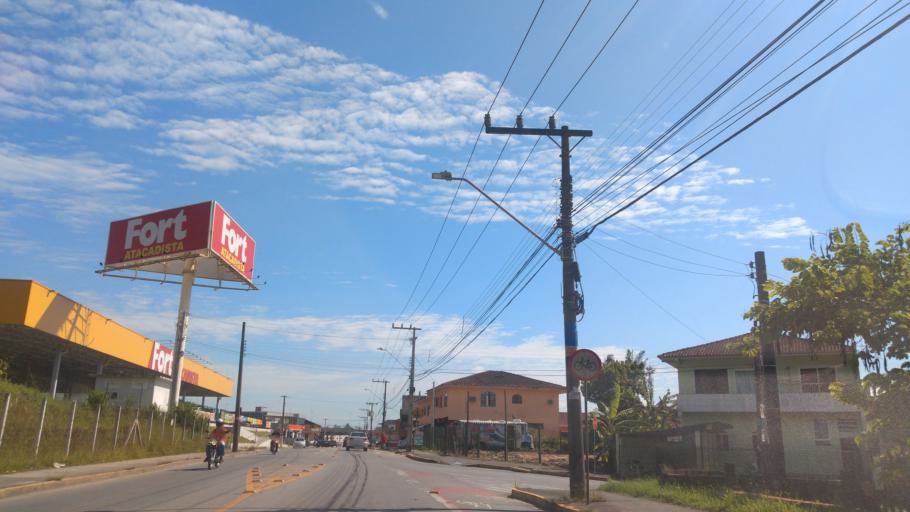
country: BR
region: Santa Catarina
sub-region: Joinville
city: Joinville
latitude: -26.2386
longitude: -48.8184
